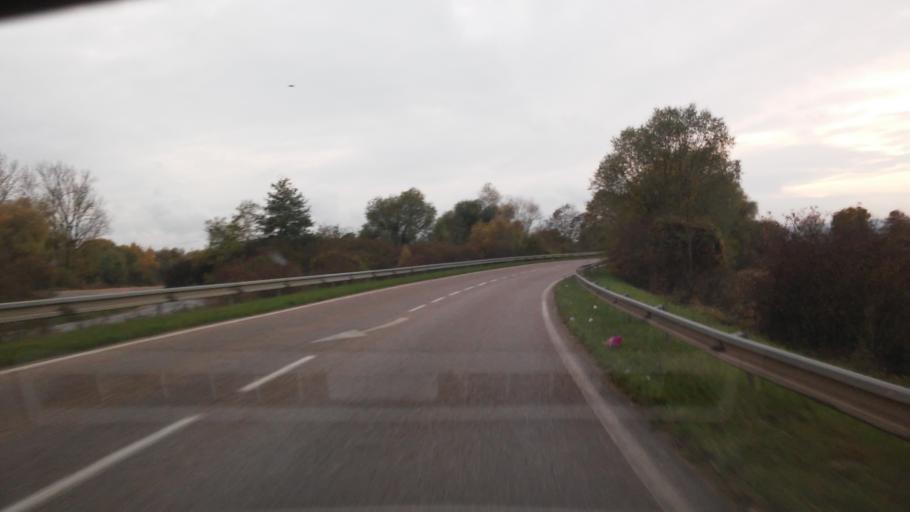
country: FR
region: Lorraine
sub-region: Departement de la Moselle
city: Ay-sur-Moselle
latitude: 49.2419
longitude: 6.1951
